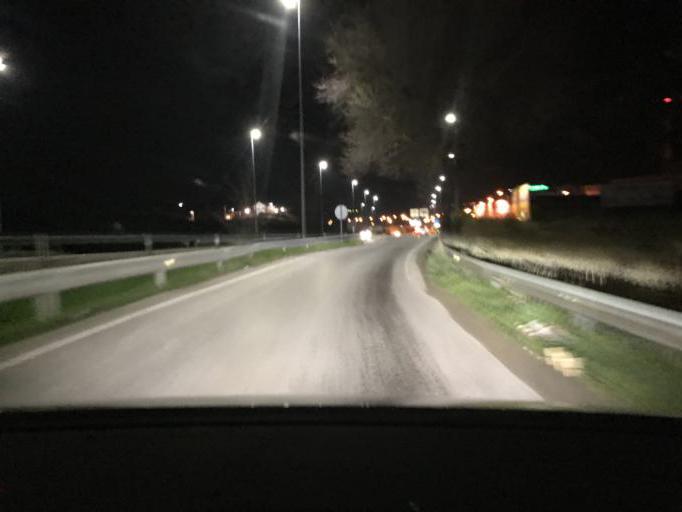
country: ES
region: Andalusia
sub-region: Provincia de Jaen
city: Jaen
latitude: 37.7815
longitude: -3.7635
